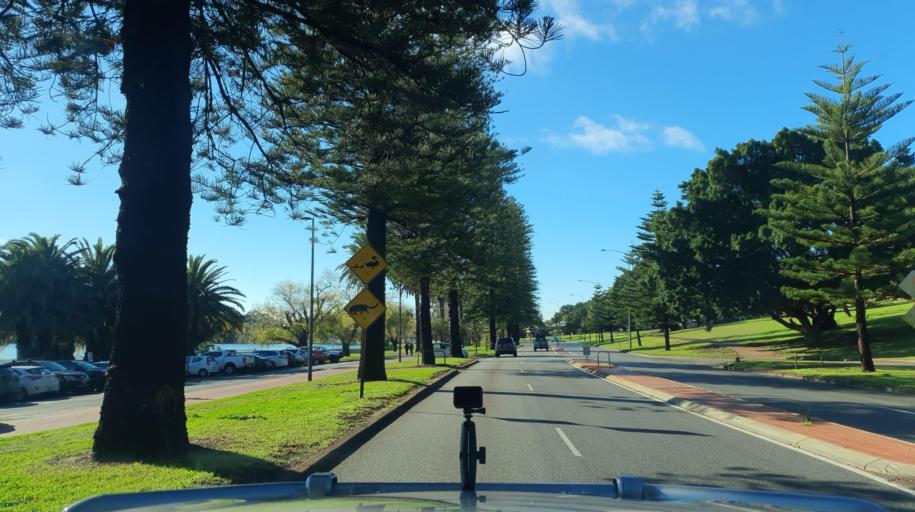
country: AU
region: Western Australia
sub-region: Cambridge
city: West Leederville
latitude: -31.9334
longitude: 115.8285
